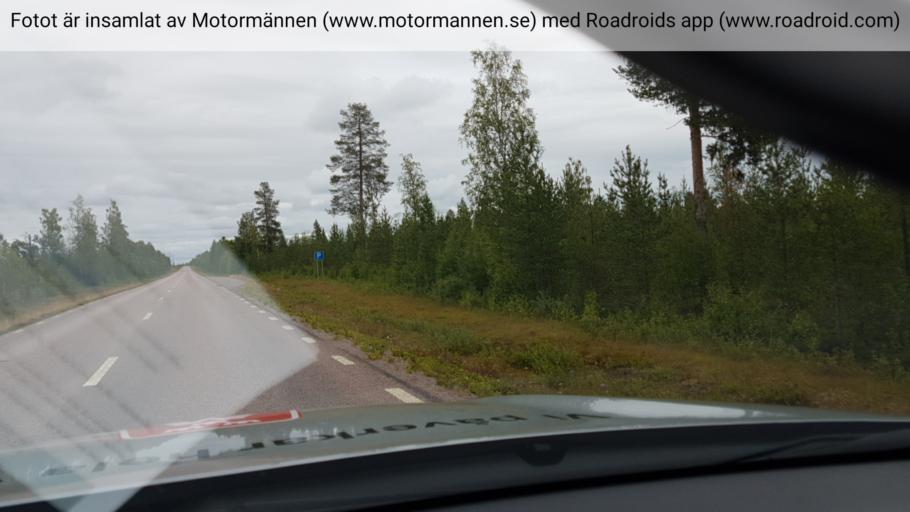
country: SE
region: Norrbotten
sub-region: Overkalix Kommun
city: OEverkalix
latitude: 67.0883
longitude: 22.5585
